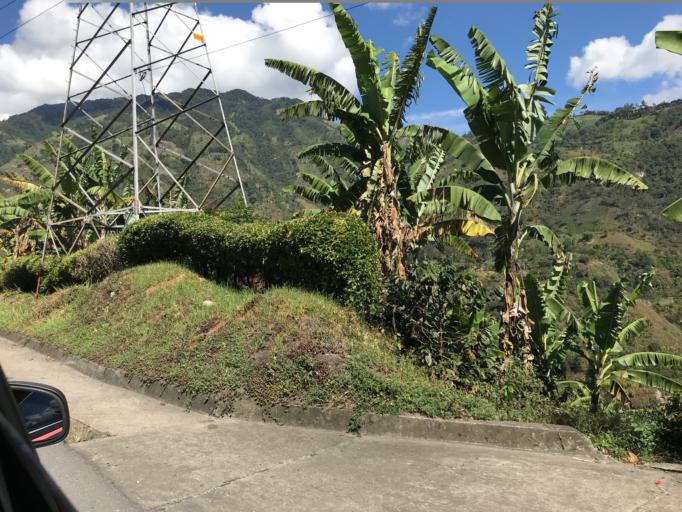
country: CO
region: Tolima
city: Cajamarca
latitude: 4.4428
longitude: -75.4082
